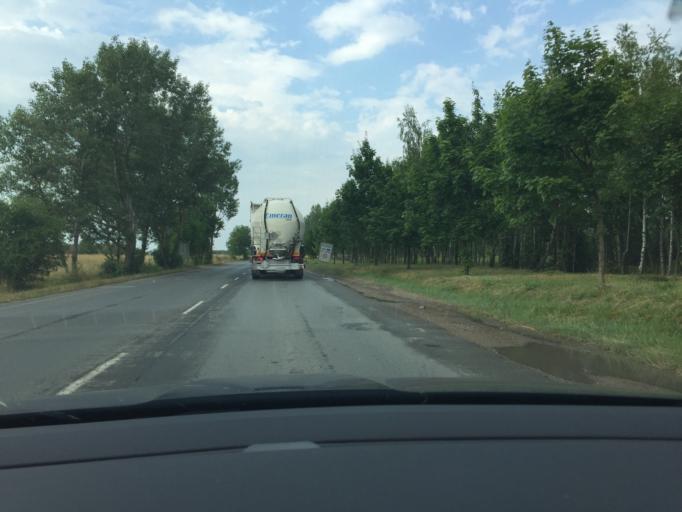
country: CZ
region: Central Bohemia
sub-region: Okres Melnik
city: Veltrusy
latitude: 50.2627
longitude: 14.3189
